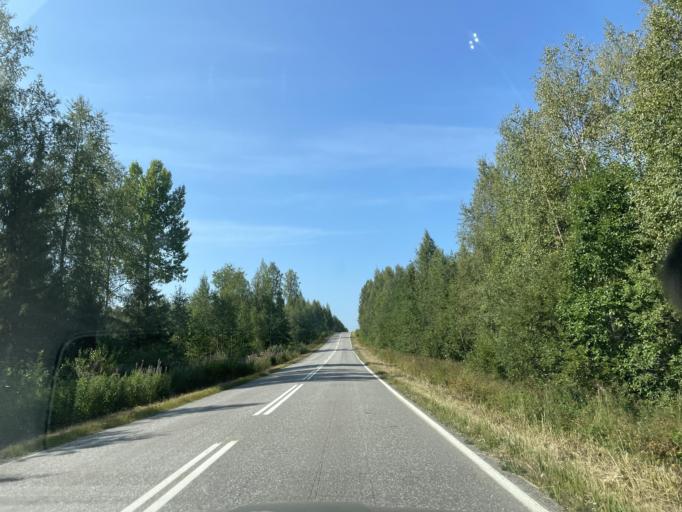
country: FI
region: Central Finland
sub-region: Saarijaervi-Viitasaari
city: Pihtipudas
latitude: 63.3666
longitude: 25.6726
